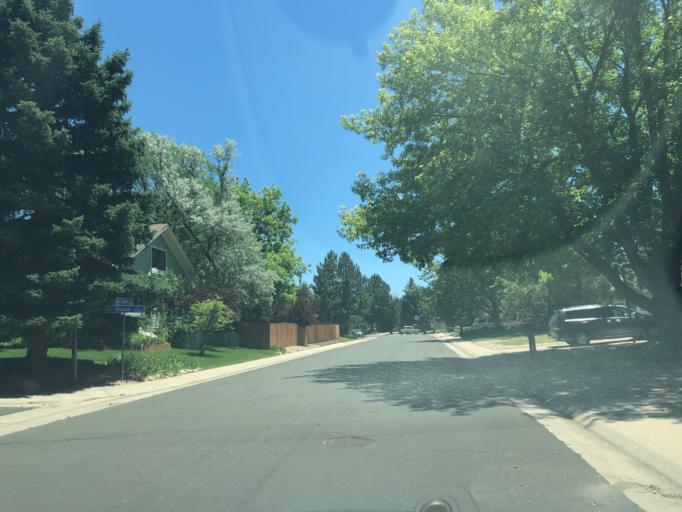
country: US
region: Colorado
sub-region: Arapahoe County
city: Dove Valley
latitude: 39.6173
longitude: -104.7799
